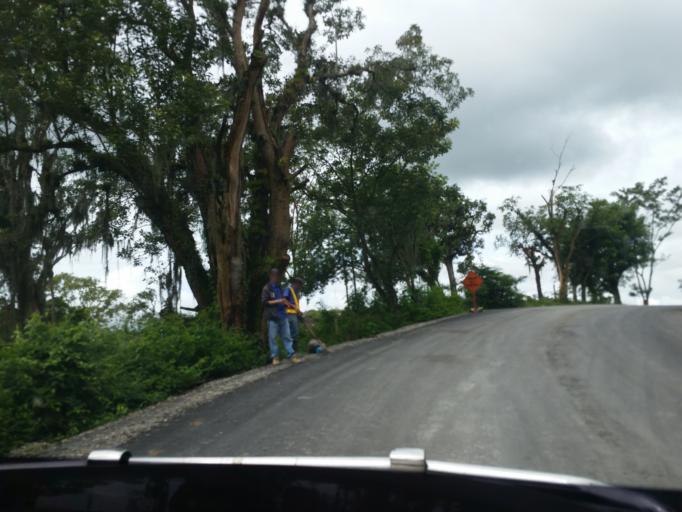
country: NI
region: Jinotega
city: Jinotega
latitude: 13.1691
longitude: -85.9226
